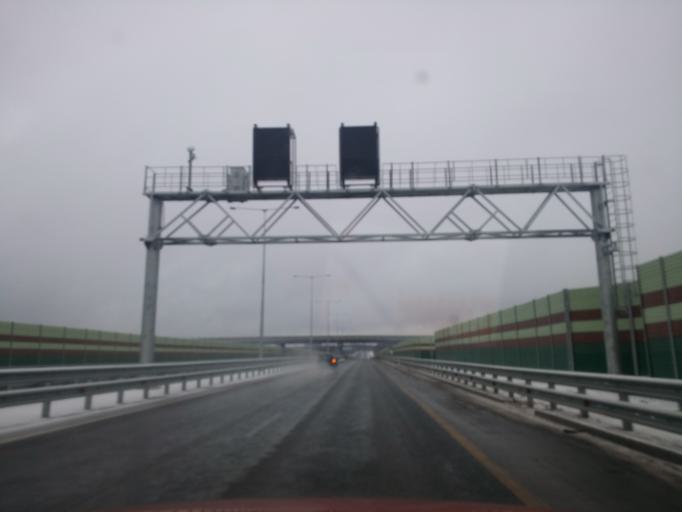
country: RU
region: Tverskaya
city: Likhoslavl'
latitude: 56.9787
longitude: 35.4322
